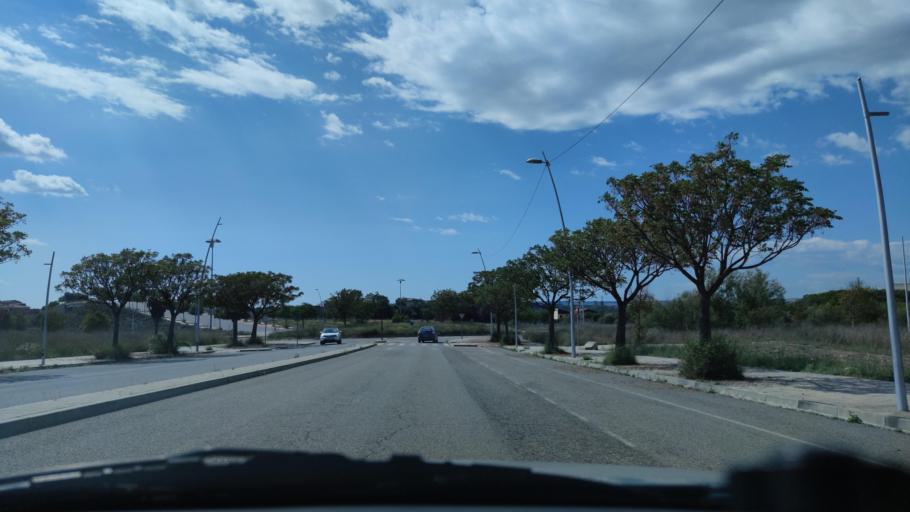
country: ES
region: Catalonia
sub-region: Provincia de Lleida
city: Lleida
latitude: 41.6070
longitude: 0.6541
